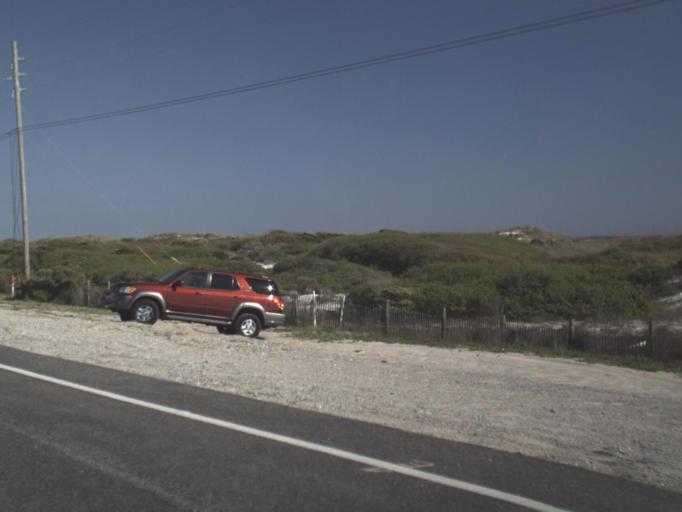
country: US
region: Florida
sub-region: Okaloosa County
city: Destin
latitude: 30.3901
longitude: -86.5390
